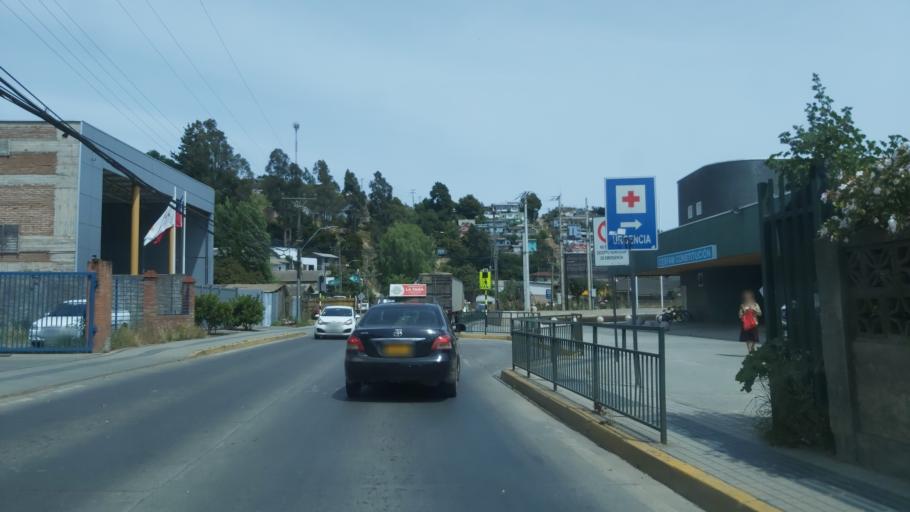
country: CL
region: Maule
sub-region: Provincia de Talca
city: Constitucion
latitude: -35.3329
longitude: -72.4167
